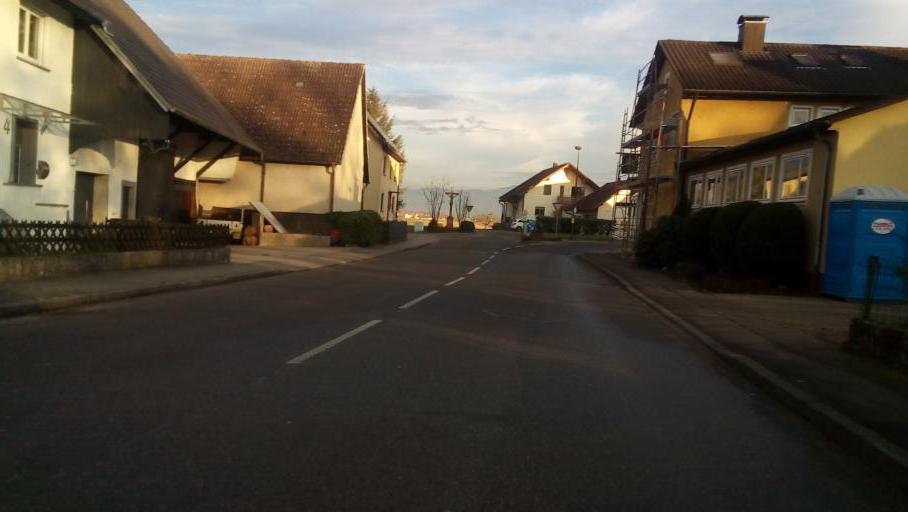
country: DE
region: Baden-Wuerttemberg
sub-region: Karlsruhe Region
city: Zell
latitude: 48.6645
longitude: 8.0179
